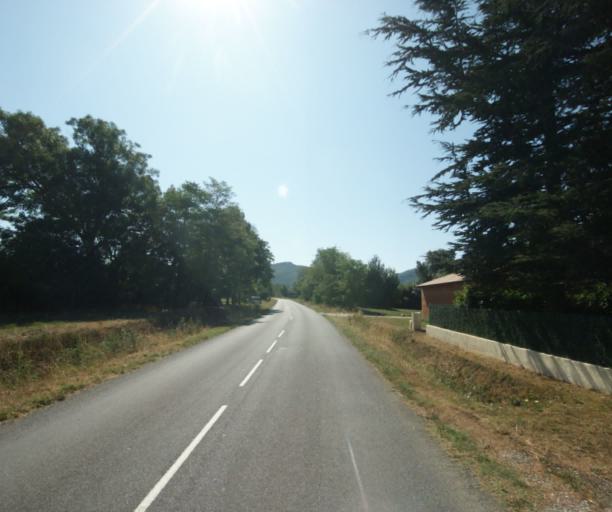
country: FR
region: Midi-Pyrenees
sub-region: Departement du Tarn
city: Soreze
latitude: 43.4587
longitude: 2.0445
